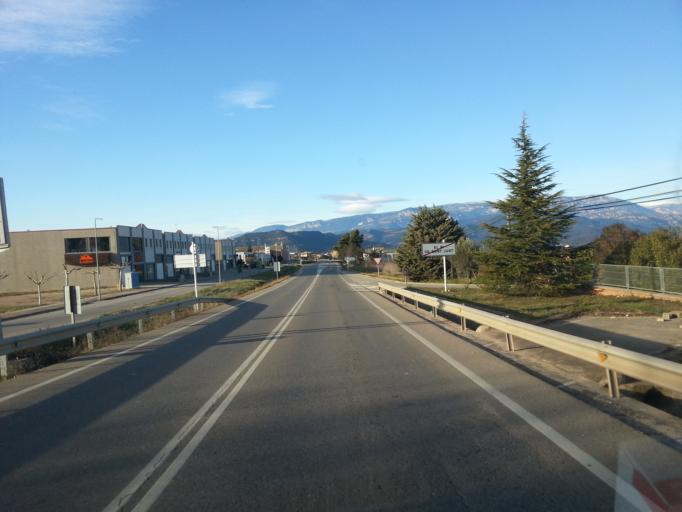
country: ES
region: Catalonia
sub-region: Provincia de Lleida
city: Olius
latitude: 41.9793
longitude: 1.5560
